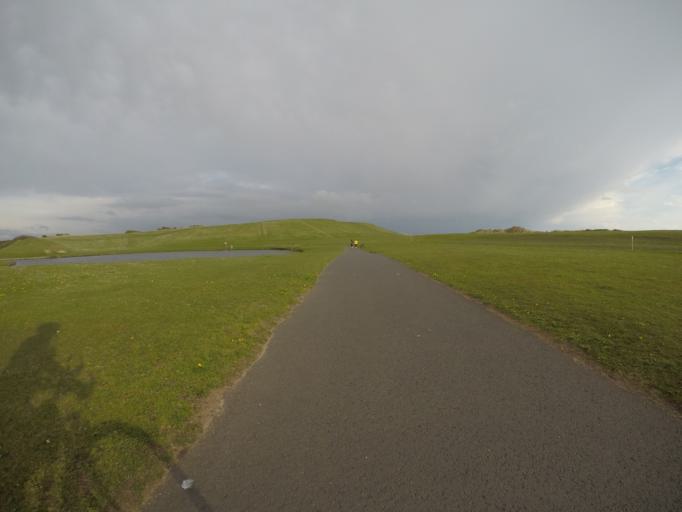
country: GB
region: Scotland
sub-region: North Ayrshire
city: Irvine
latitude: 55.6034
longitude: -4.6892
